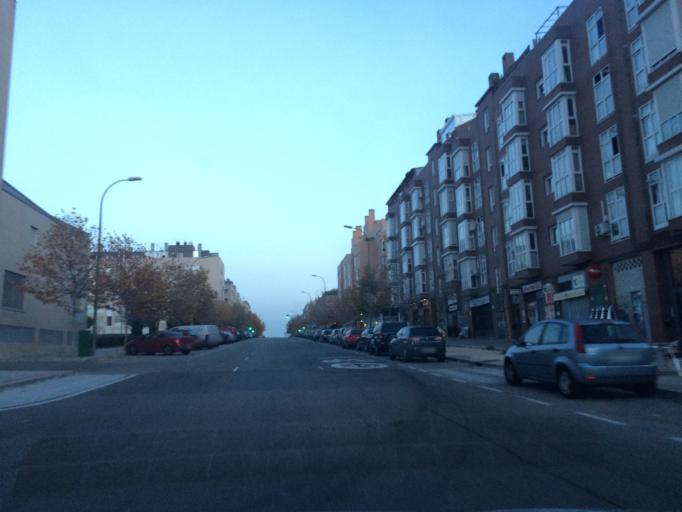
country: ES
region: Madrid
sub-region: Provincia de Madrid
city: Fuencarral-El Pardo
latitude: 40.5037
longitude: -3.7091
